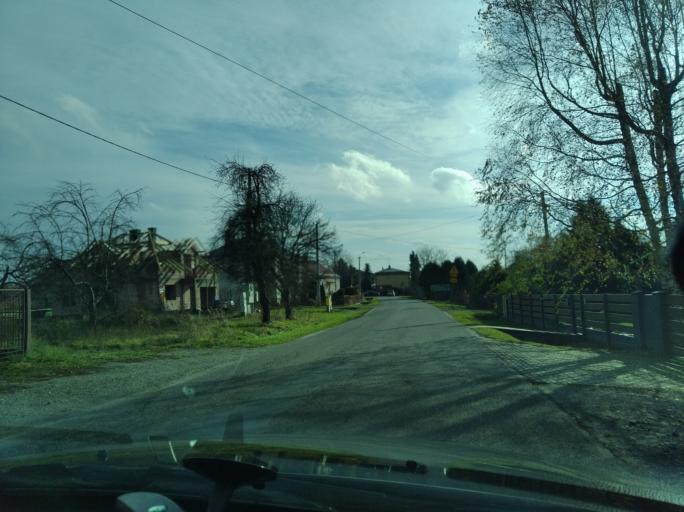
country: PL
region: Subcarpathian Voivodeship
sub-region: Powiat ropczycko-sedziszowski
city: Sedziszow Malopolski
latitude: 50.1022
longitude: 21.7345
